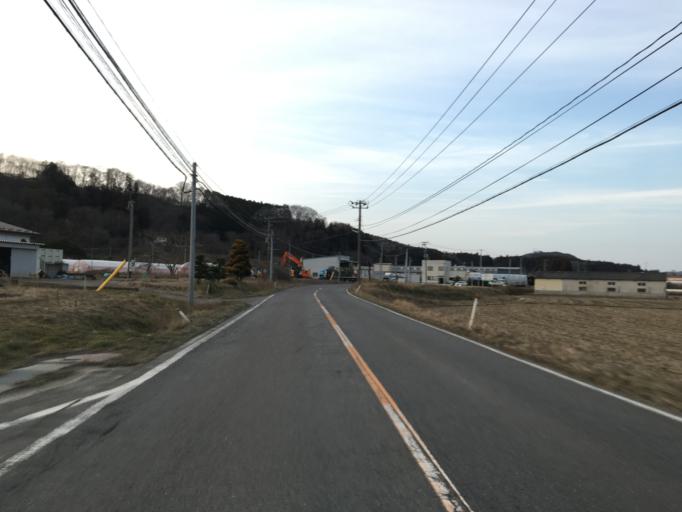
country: JP
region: Ibaraki
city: Daigo
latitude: 36.9373
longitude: 140.4058
